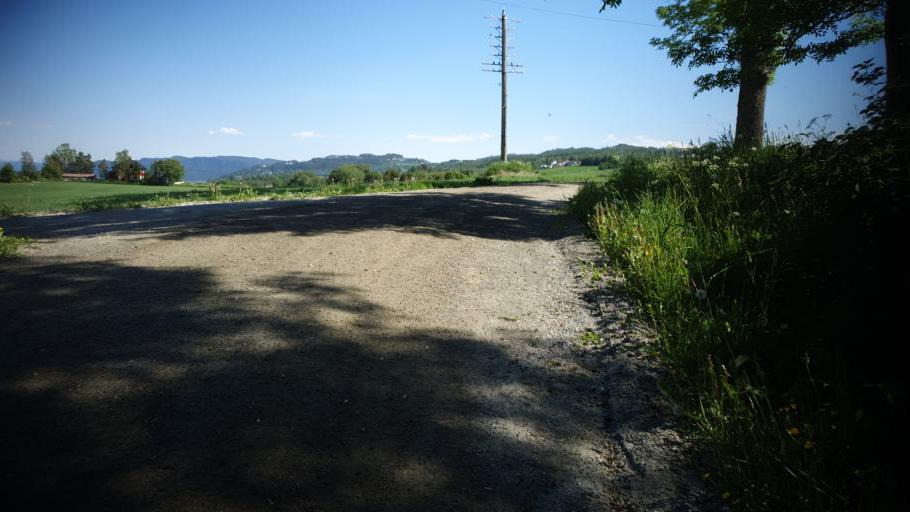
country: NO
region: Sor-Trondelag
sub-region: Malvik
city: Malvik
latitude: 63.4369
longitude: 10.6717
